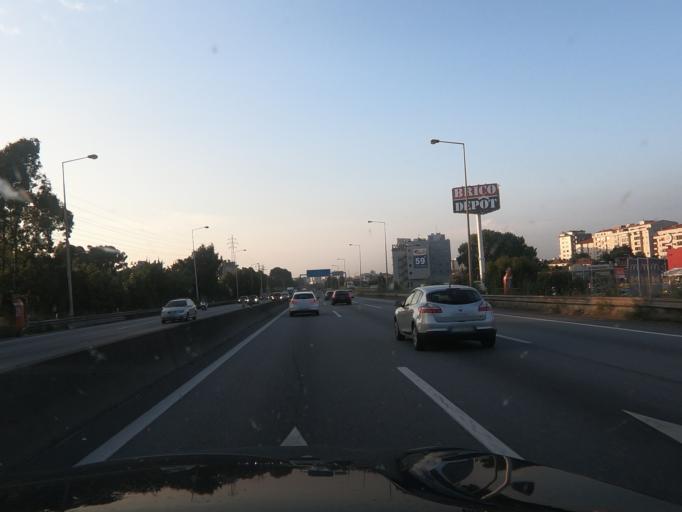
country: PT
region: Porto
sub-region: Vila Nova de Gaia
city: Canidelo
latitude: 41.1246
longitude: -8.6357
